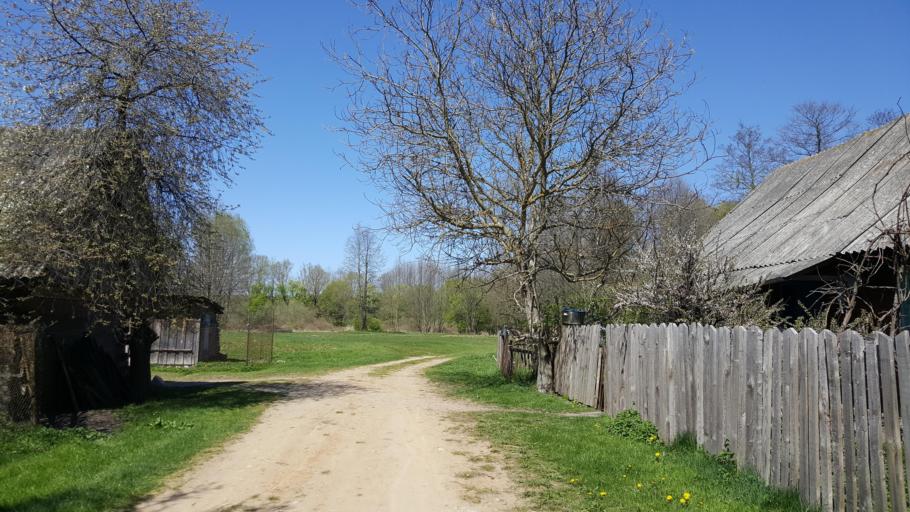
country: BY
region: Brest
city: Kamyanyets
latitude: 52.3386
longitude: 23.7434
